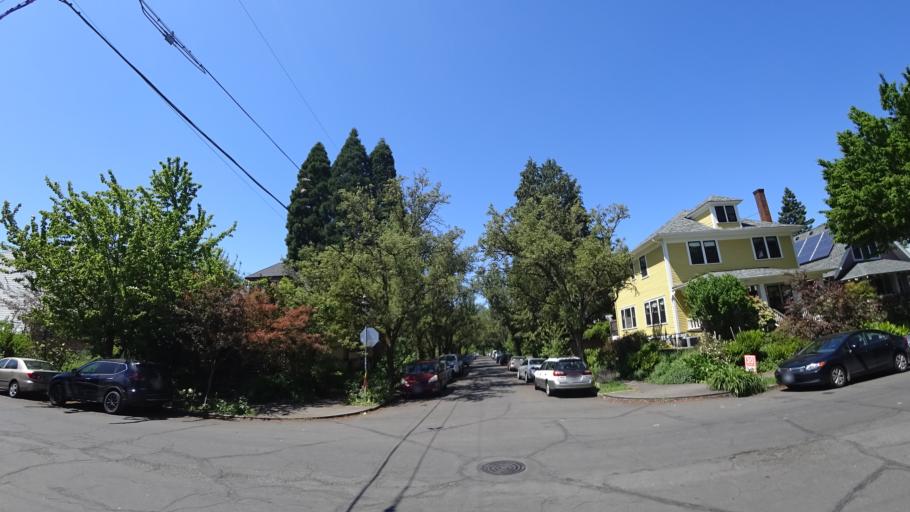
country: US
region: Oregon
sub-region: Multnomah County
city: Portland
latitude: 45.5055
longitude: -122.6326
